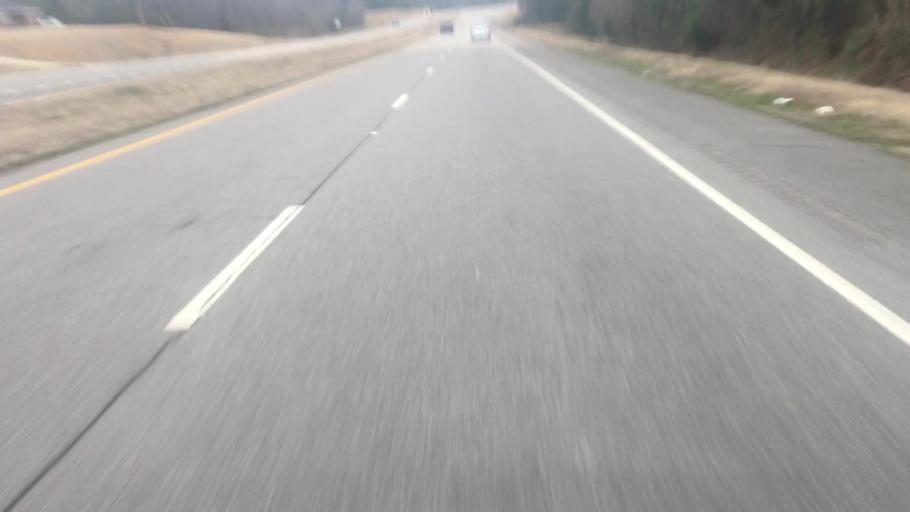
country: US
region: Alabama
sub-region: Walker County
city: Cordova
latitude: 33.8213
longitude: -87.1624
